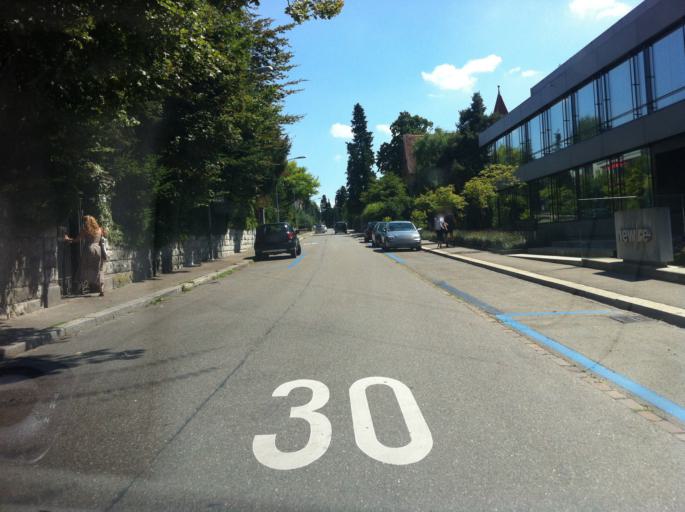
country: CH
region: Zurich
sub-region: Bezirk Zuerich
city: Zuerich (Kreis 8) / Weinegg
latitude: 47.3494
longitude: 8.5649
